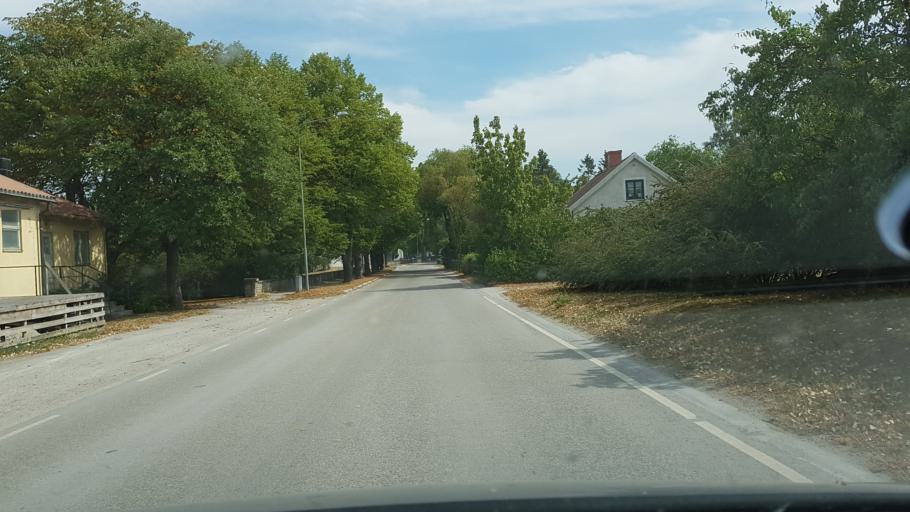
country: SE
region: Gotland
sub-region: Gotland
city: Slite
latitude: 57.7087
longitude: 18.8005
